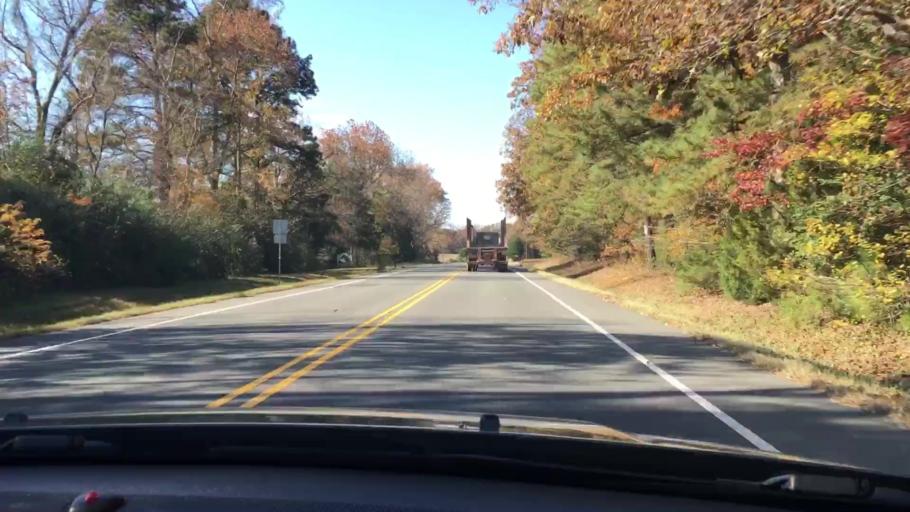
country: US
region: Virginia
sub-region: King William County
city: Central Garage
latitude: 37.7754
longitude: -77.1597
